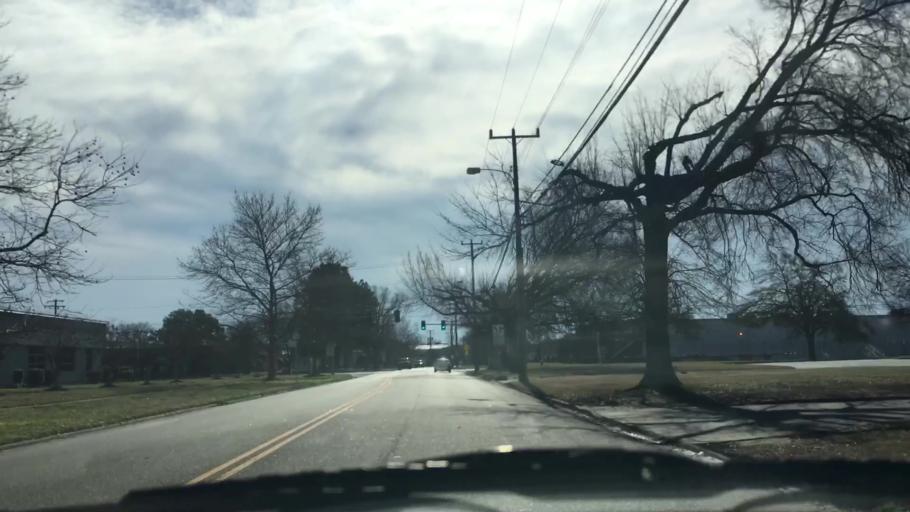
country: US
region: Virginia
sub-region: City of Norfolk
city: Norfolk
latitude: 36.8626
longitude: -76.2345
